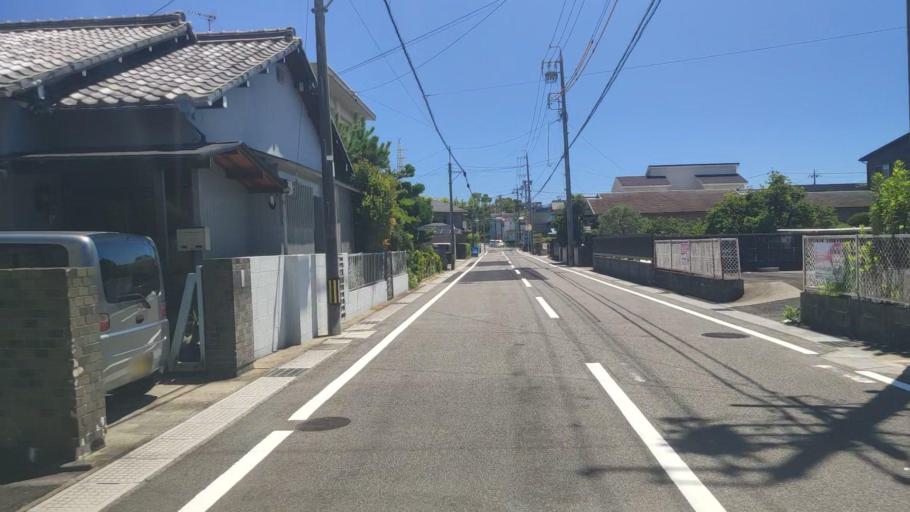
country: JP
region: Mie
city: Suzuka
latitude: 34.8546
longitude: 136.5869
